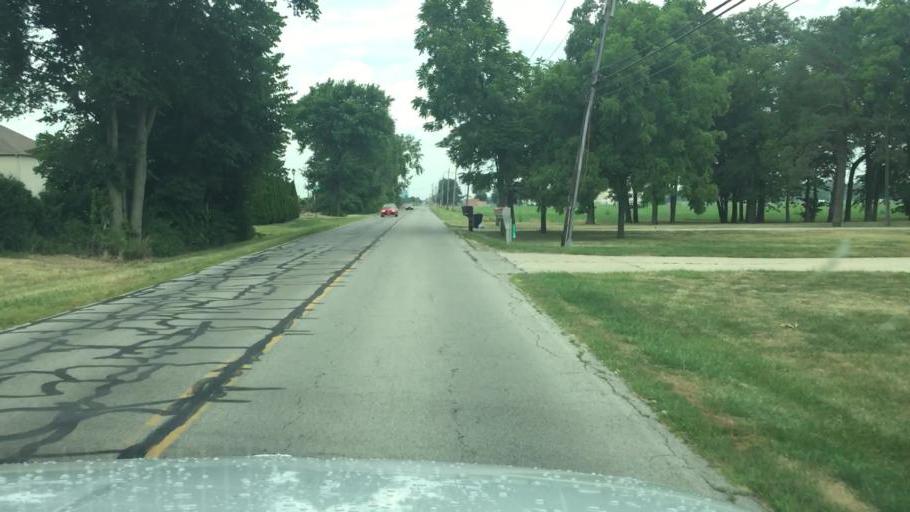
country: US
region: Ohio
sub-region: Wood County
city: Walbridge
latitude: 41.5823
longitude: -83.5278
